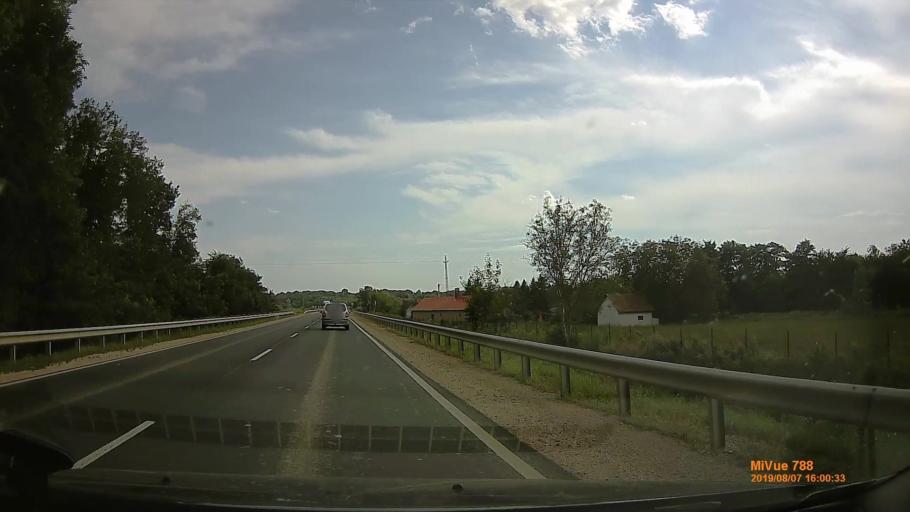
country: HU
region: Vas
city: Kormend
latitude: 47.0001
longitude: 16.6155
